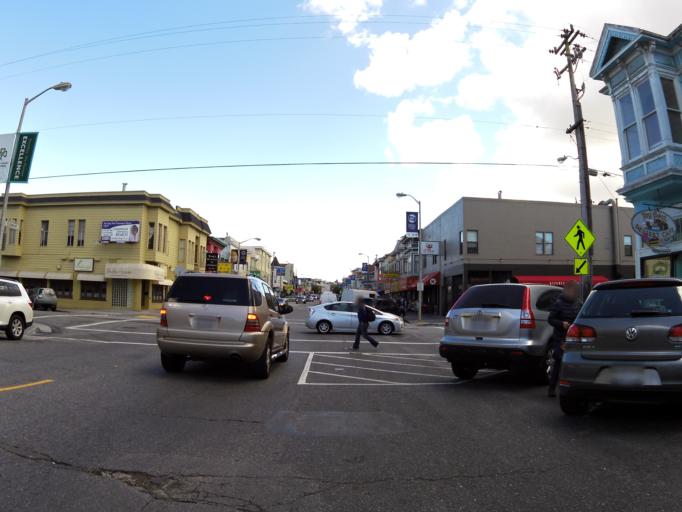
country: US
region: California
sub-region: San Francisco County
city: San Francisco
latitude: 37.7830
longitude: -122.4637
